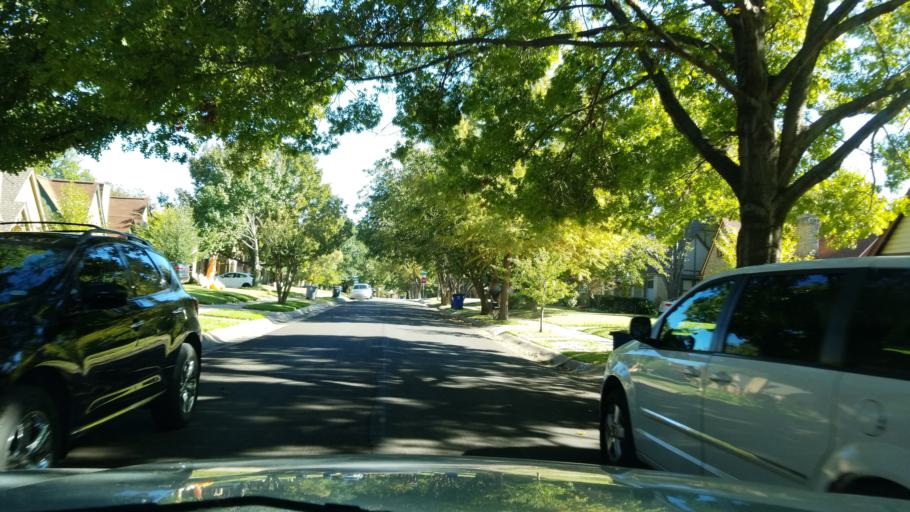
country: US
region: Texas
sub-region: Dallas County
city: Highland Park
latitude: 32.8048
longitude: -96.7431
